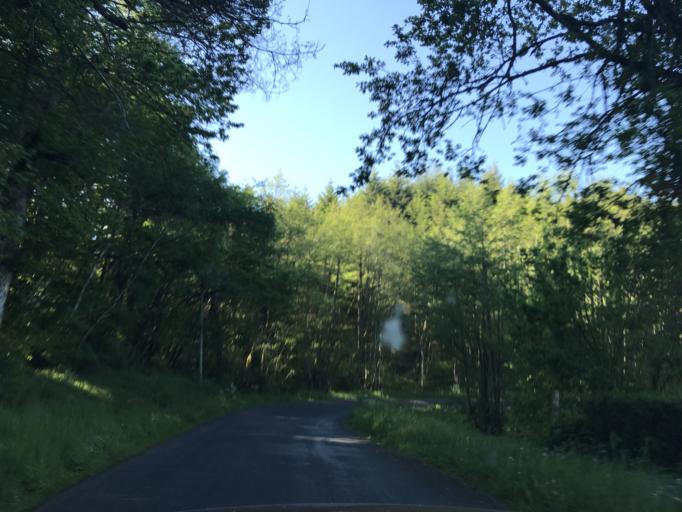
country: FR
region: Auvergne
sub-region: Departement du Puy-de-Dome
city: Job
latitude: 45.6979
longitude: 3.6928
